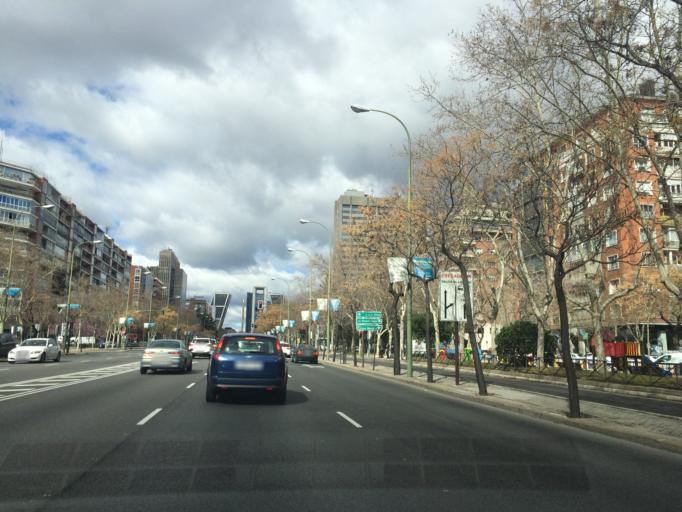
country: ES
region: Madrid
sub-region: Provincia de Madrid
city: Chamartin
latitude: 40.4550
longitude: -3.6903
